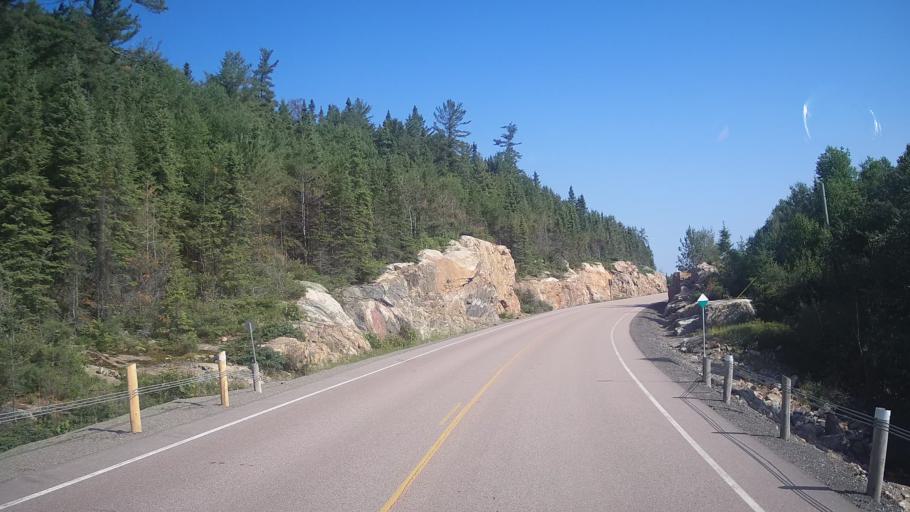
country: CA
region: Ontario
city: Rayside-Balfour
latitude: 47.0184
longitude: -81.6381
